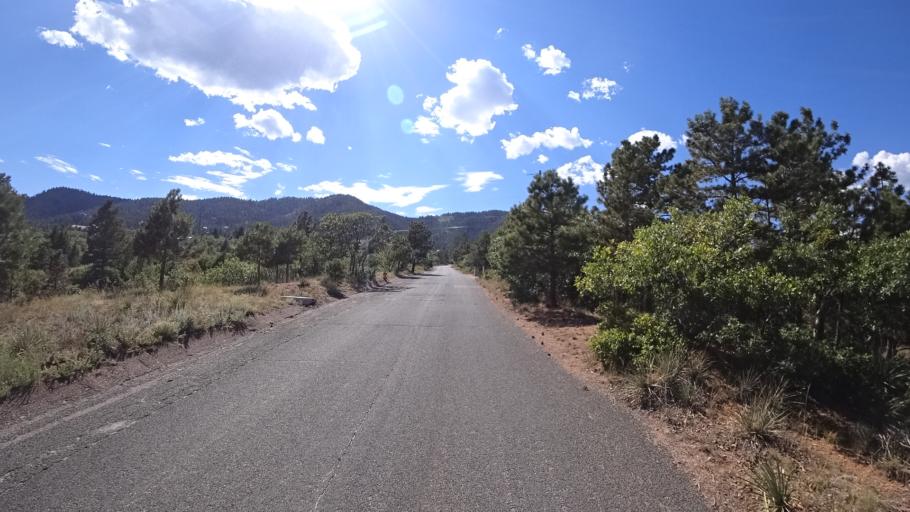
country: US
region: Colorado
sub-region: El Paso County
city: Colorado Springs
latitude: 38.8135
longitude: -104.8737
